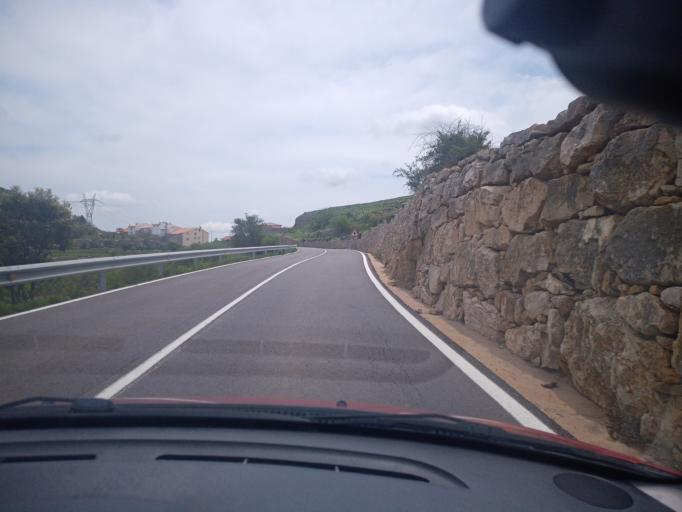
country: ES
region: Valencia
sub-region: Provincia de Castello
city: Ares del Maestre
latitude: 40.4561
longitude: -0.1450
